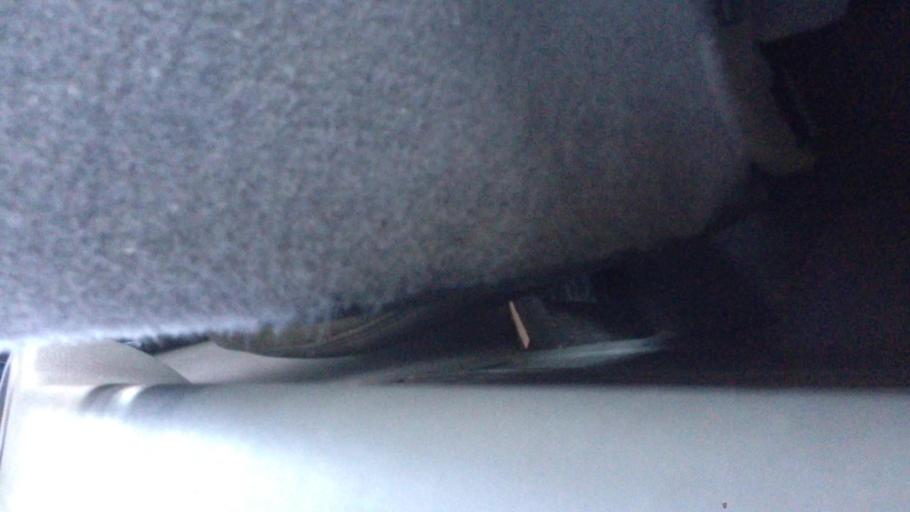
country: US
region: New York
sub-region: Dutchess County
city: Tivoli
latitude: 42.0833
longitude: -73.8284
